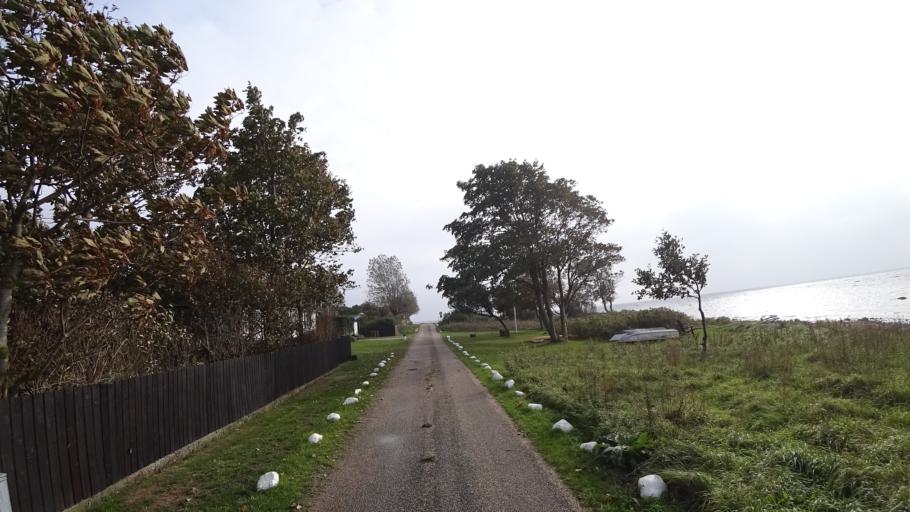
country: SE
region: Skane
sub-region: Kavlinge Kommun
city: Hofterup
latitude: 55.7298
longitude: 12.9542
